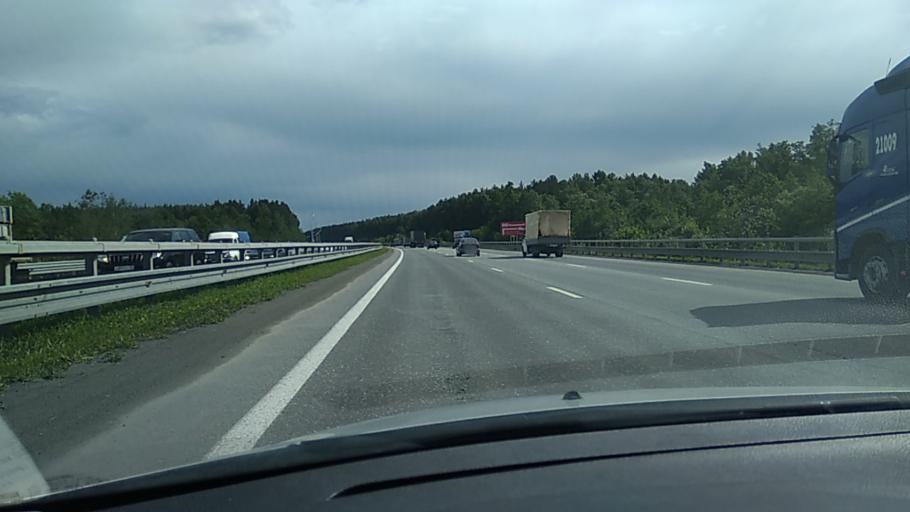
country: RU
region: Sverdlovsk
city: Shuvakish
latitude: 56.9164
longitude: 60.5081
